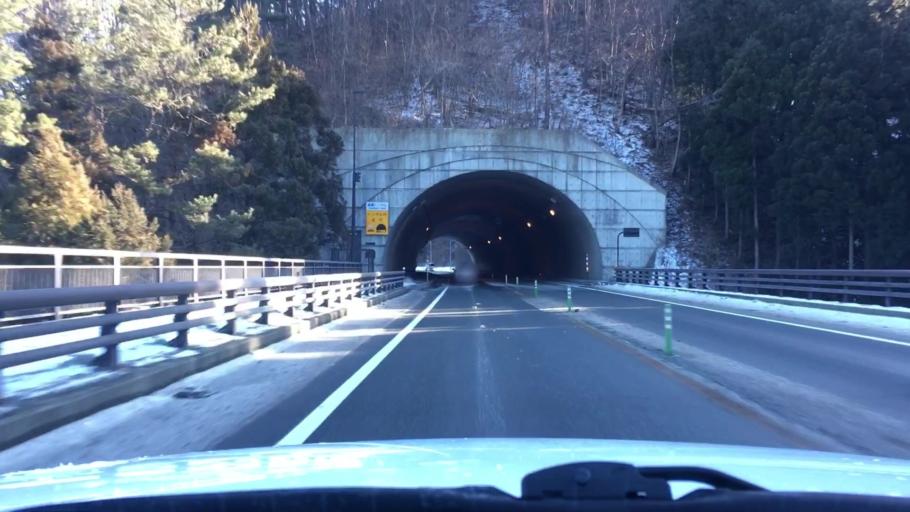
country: JP
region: Iwate
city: Morioka-shi
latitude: 39.6721
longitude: 141.2743
